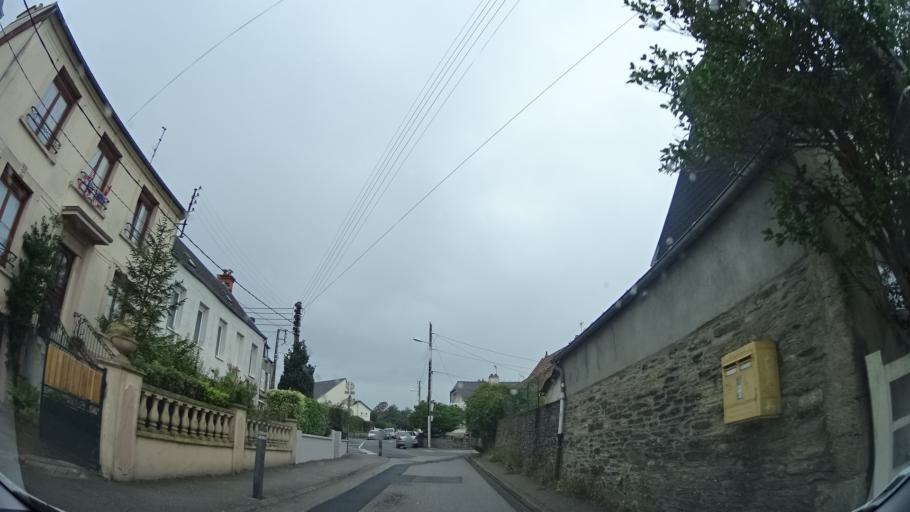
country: FR
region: Lower Normandy
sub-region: Departement de la Manche
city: Octeville
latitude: 49.6320
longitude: -1.6349
